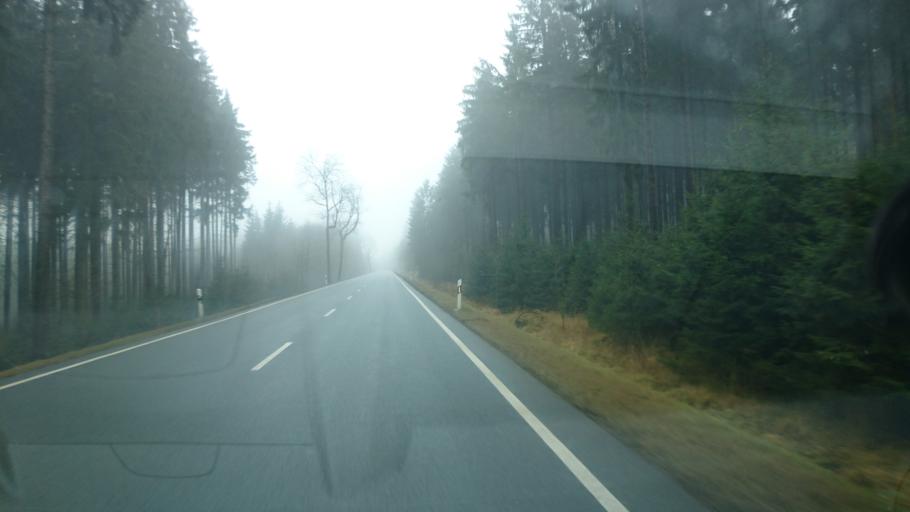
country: DE
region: Thuringia
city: Tanna
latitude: 50.4760
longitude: 11.8387
